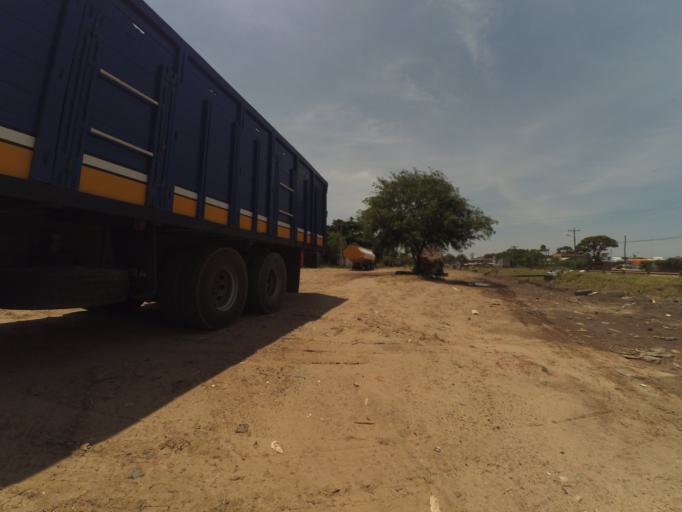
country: BO
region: Santa Cruz
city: Santa Cruz de la Sierra
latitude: -17.8357
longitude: -63.2390
